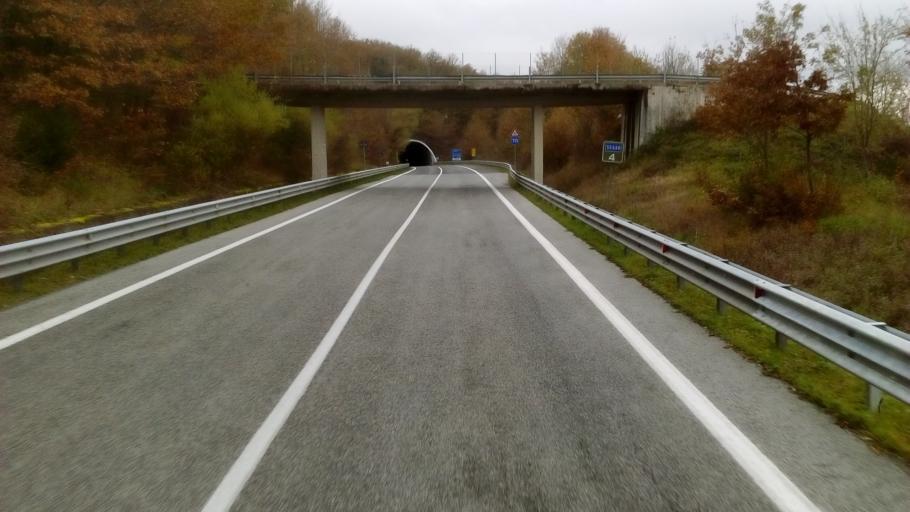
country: IT
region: Molise
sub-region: Provincia di Isernia
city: Chiauci
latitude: 41.6722
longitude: 14.3606
